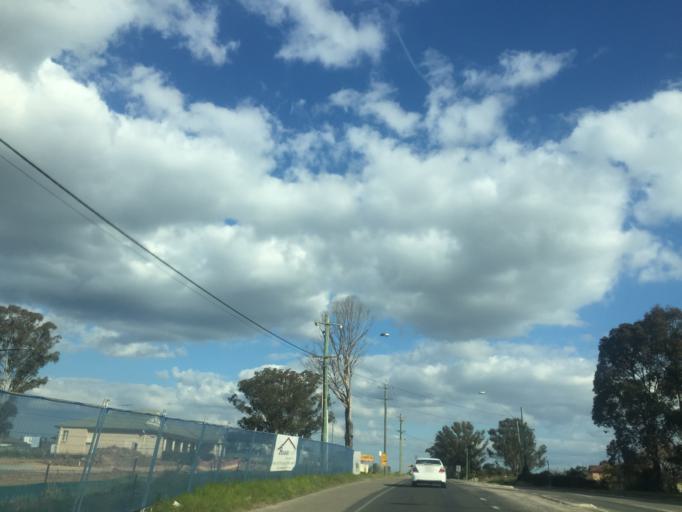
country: AU
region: New South Wales
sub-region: Blacktown
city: Quakers Hill
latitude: -33.7059
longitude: 150.8939
